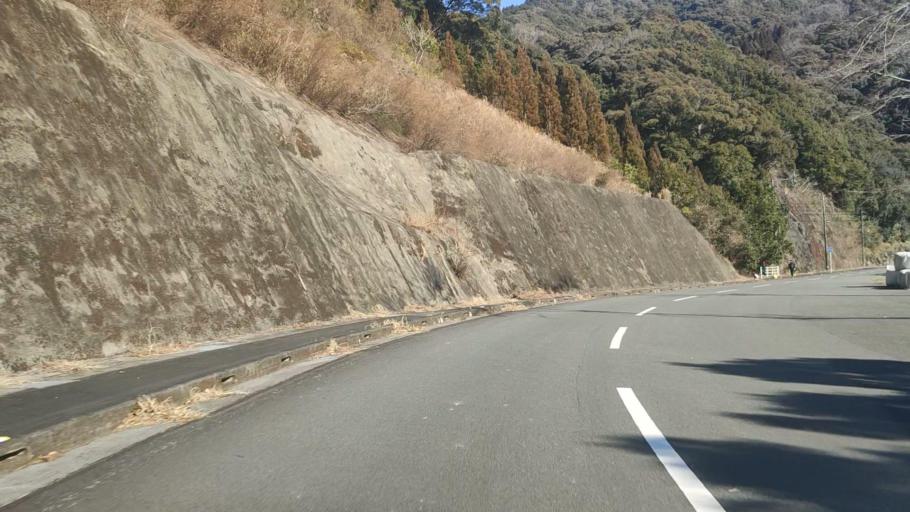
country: JP
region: Oita
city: Saiki
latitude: 32.7741
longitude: 131.8213
